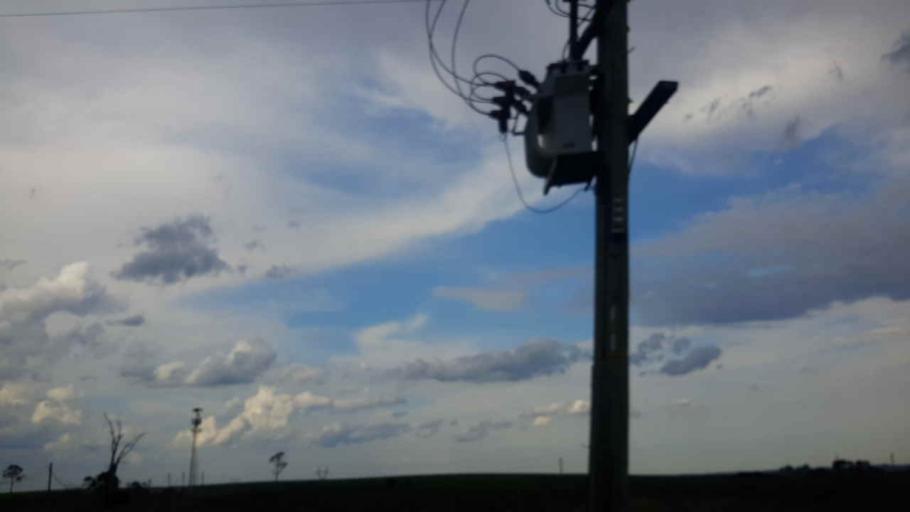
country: AU
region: New South Wales
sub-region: Liverpool
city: Luddenham
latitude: -33.8603
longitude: 150.6978
